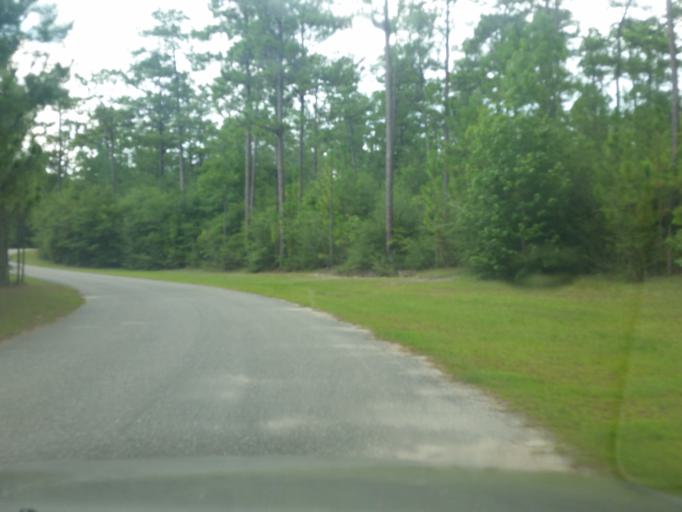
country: US
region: Alabama
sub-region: Baldwin County
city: Spanish Fort
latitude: 30.7369
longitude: -87.9061
